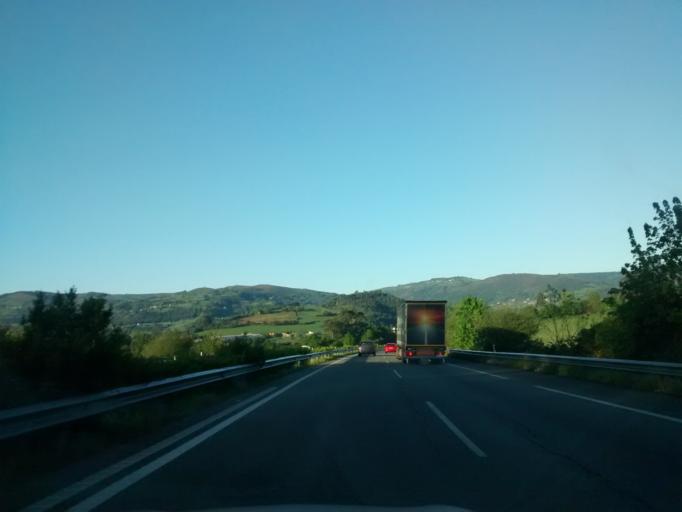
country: ES
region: Asturias
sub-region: Province of Asturias
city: Villaviciosa
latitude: 43.4762
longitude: -5.4622
